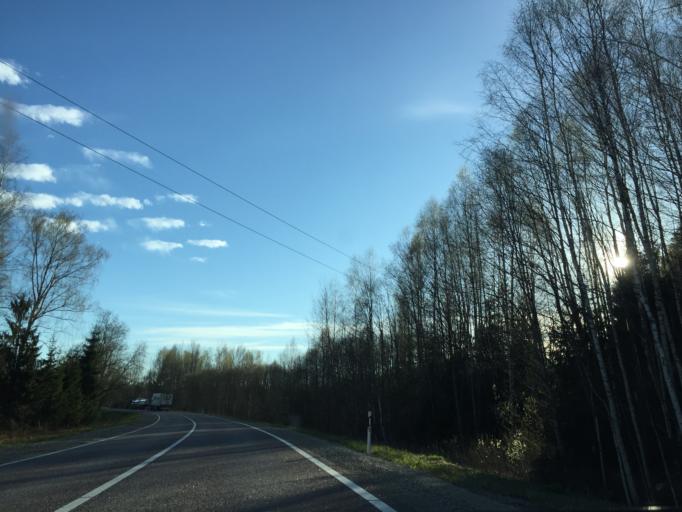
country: LV
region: Valkas Rajons
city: Valka
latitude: 57.7103
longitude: 25.9136
